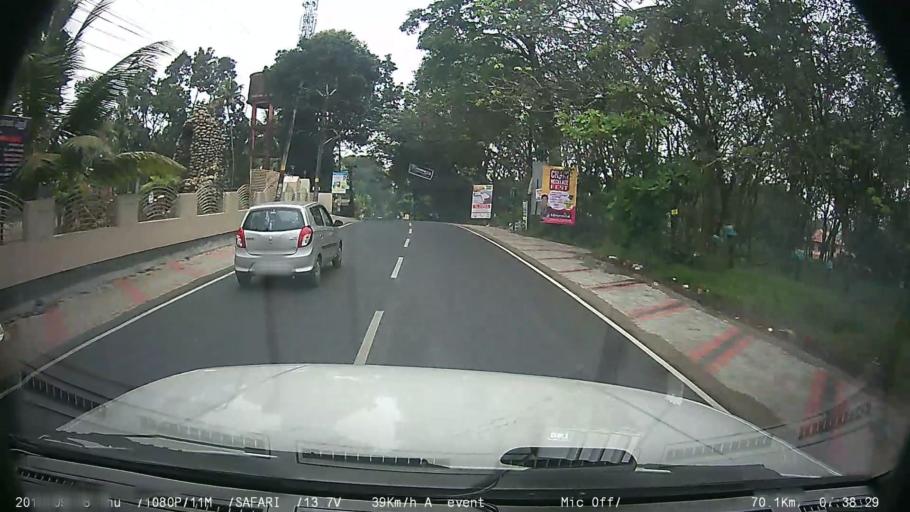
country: IN
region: Kerala
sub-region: Kottayam
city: Changanacheri
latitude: 9.4395
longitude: 76.5680
